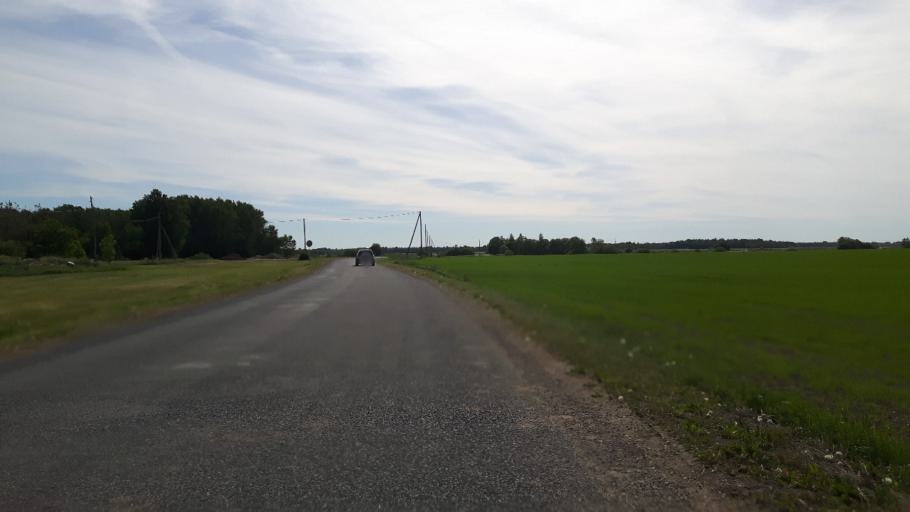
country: EE
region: Harju
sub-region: Raasiku vald
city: Arukula
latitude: 59.4246
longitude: 25.0879
